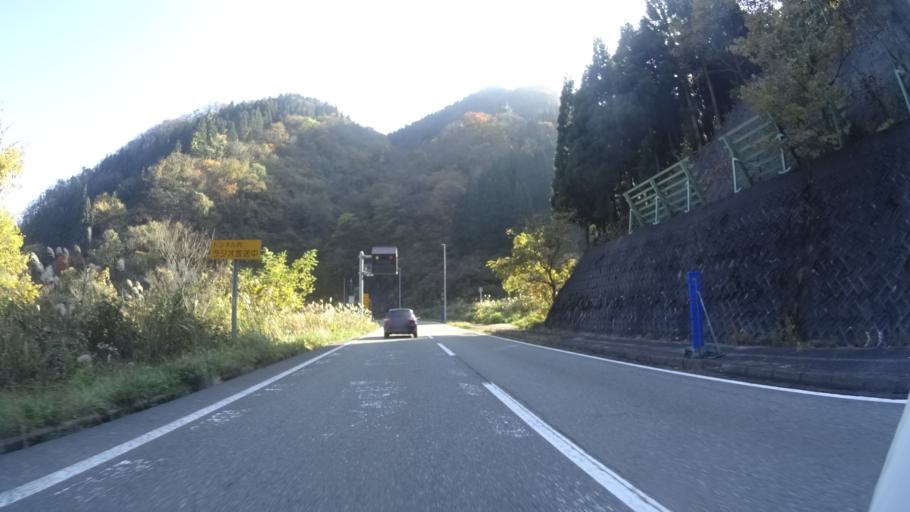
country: JP
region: Fukui
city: Ono
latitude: 35.9623
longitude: 136.6057
